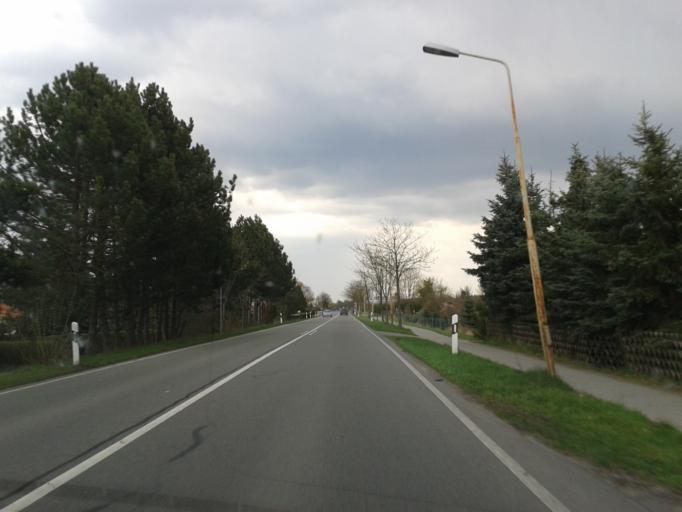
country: DE
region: Saxony-Anhalt
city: Salzwedel
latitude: 52.8606
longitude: 11.1197
